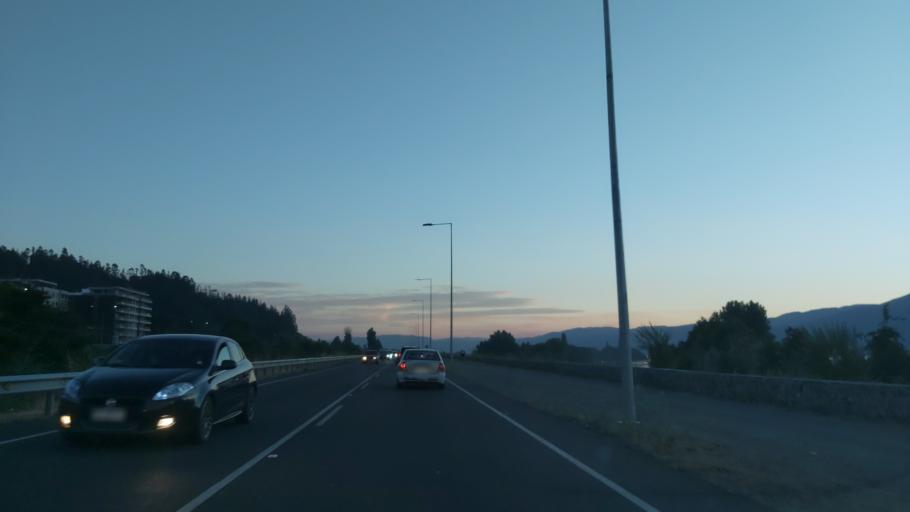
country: CL
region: Biobio
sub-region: Provincia de Concepcion
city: Chiguayante
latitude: -36.8803
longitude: -73.0389
